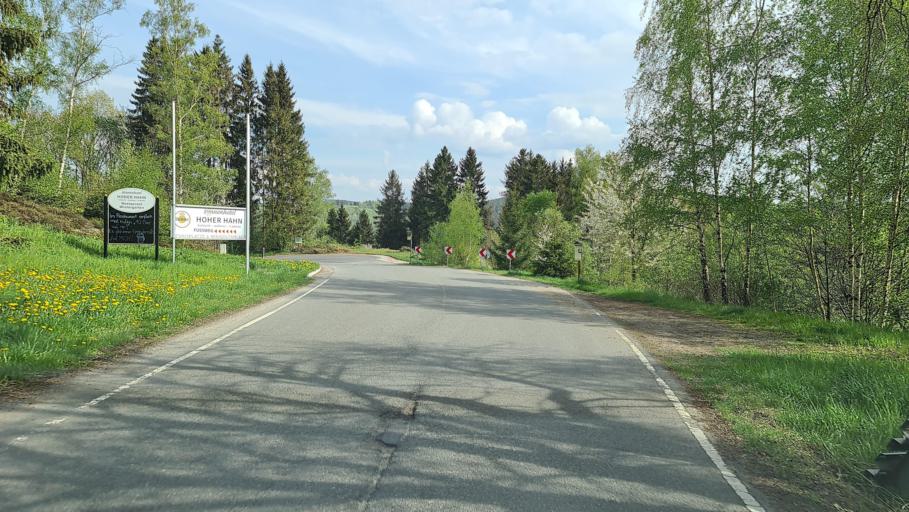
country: DE
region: Saxony
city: Schwarzenberg
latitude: 50.5166
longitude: 12.7660
